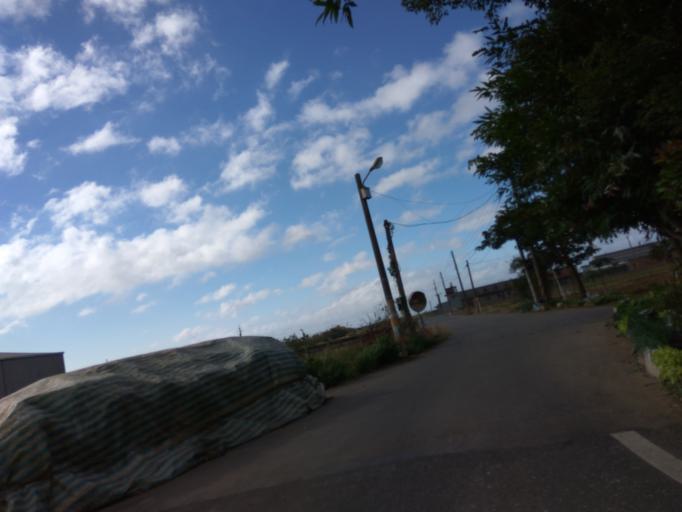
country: TW
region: Taiwan
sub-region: Hsinchu
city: Zhubei
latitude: 24.9741
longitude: 121.0724
